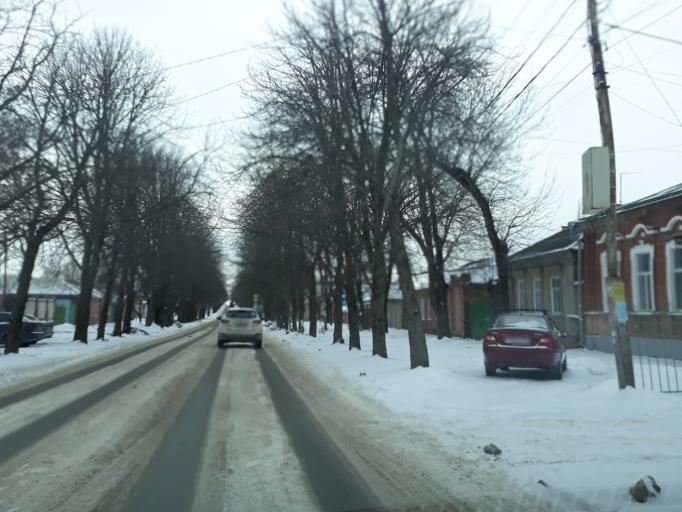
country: RU
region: Rostov
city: Taganrog
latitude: 47.2073
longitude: 38.9218
